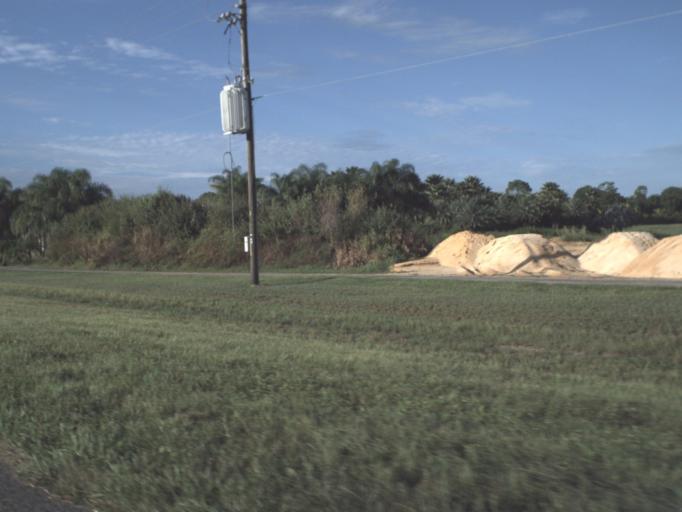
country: US
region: Florida
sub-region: Highlands County
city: Lake Placid
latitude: 27.3455
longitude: -81.3872
